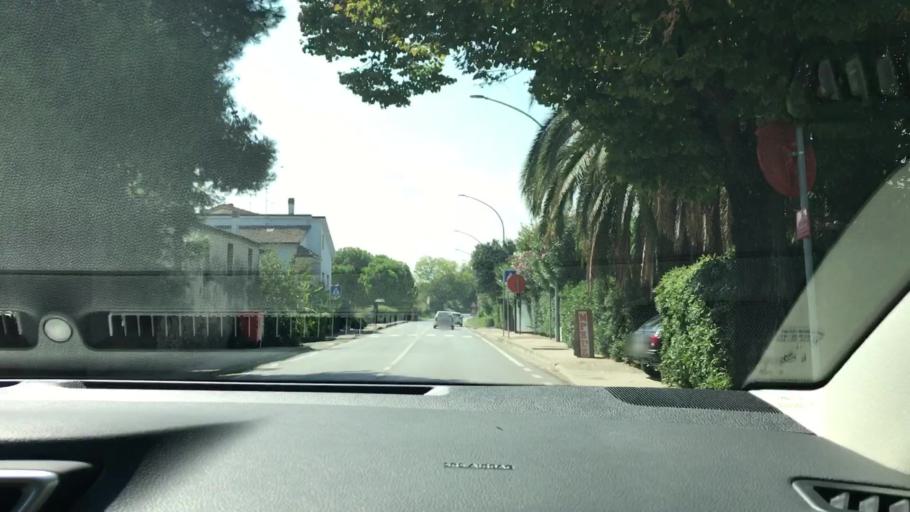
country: IT
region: The Marches
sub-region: Provincia di Ascoli Piceno
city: San Benedetto del Tronto
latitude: 42.9055
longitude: 13.8670
